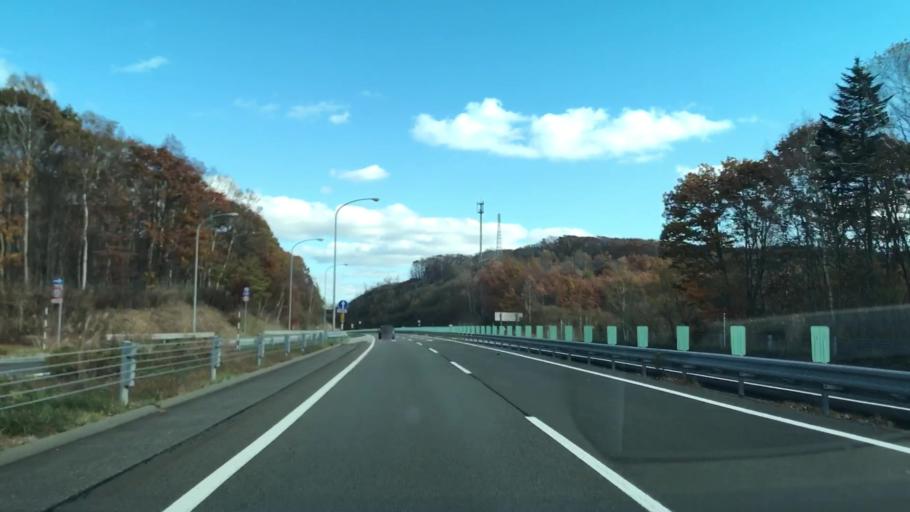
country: JP
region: Hokkaido
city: Chitose
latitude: 42.8772
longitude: 141.7340
